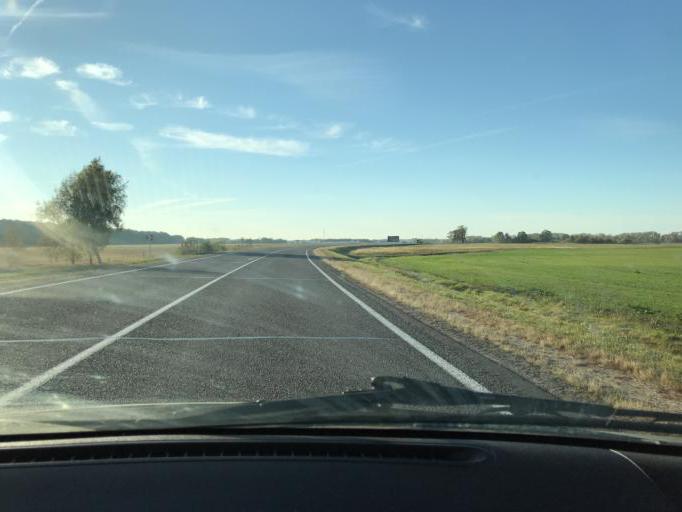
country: BY
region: Brest
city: Horad Kobryn
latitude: 52.2097
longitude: 24.4718
